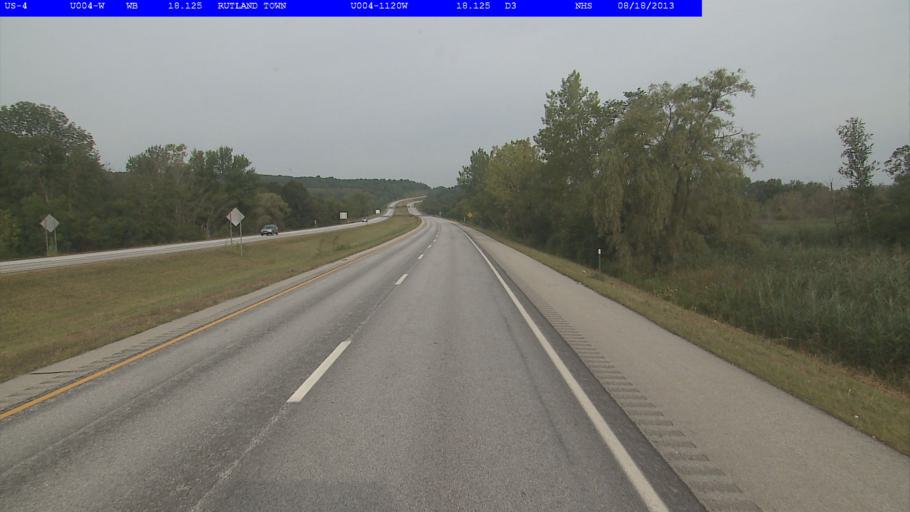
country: US
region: Vermont
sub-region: Rutland County
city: Rutland
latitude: 43.5827
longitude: -72.9796
